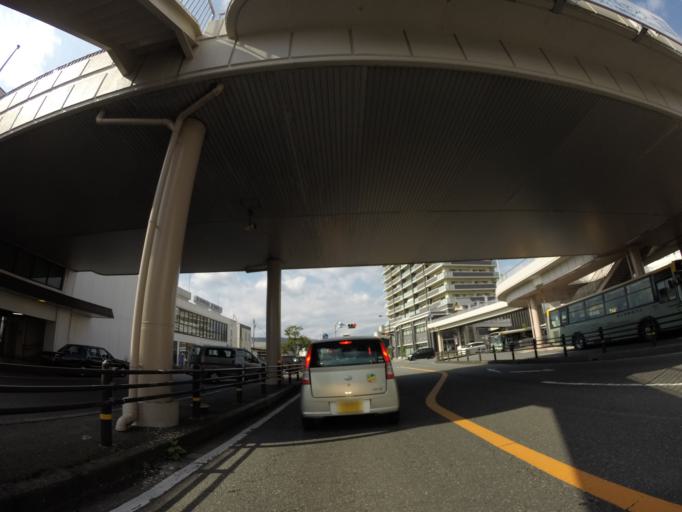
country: JP
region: Shizuoka
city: Fujinomiya
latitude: 35.2216
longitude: 138.6150
